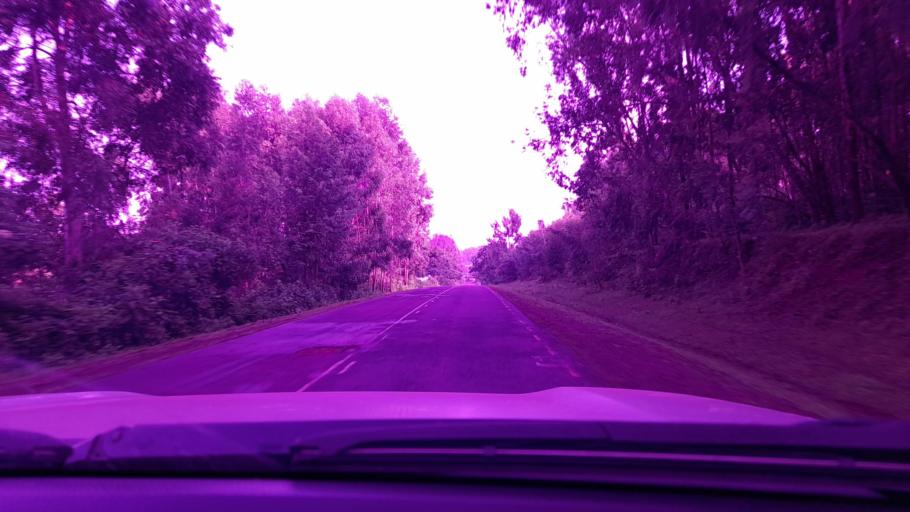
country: ET
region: Oromiya
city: Bedele
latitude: 8.1627
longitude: 36.4742
